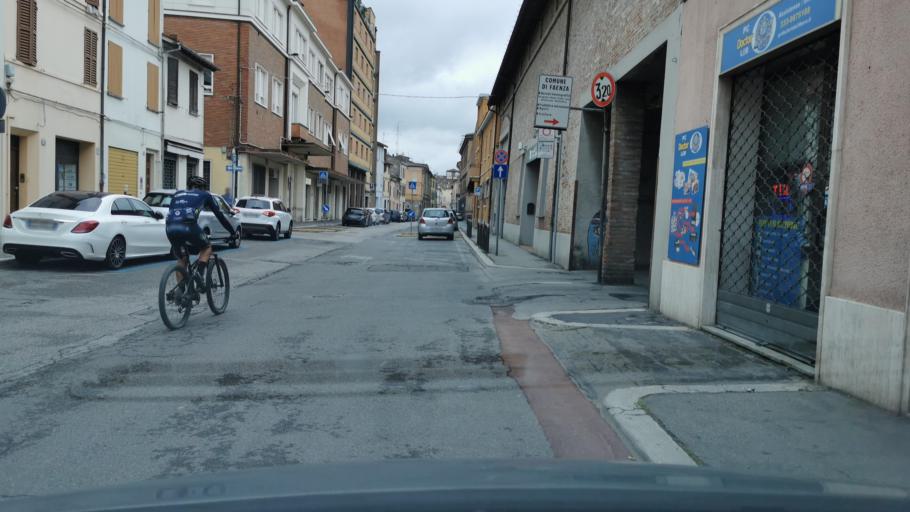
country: IT
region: Emilia-Romagna
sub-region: Provincia di Ravenna
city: Faenza
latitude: 44.2895
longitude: 11.8843
